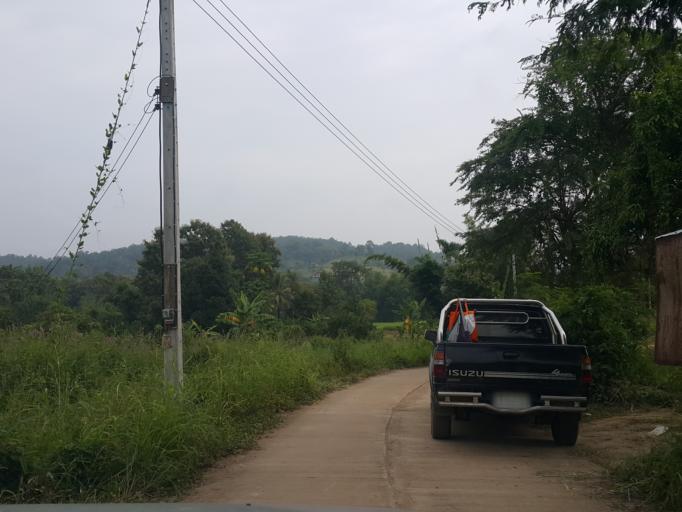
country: TH
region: Mae Hong Son
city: Wiang Nuea
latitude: 19.3794
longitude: 98.4582
